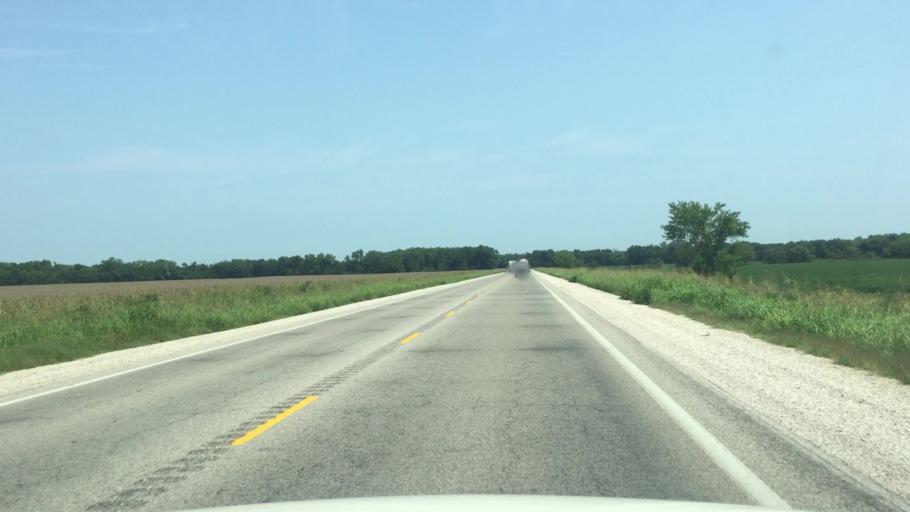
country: US
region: Kansas
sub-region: Montgomery County
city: Cherryvale
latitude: 37.1691
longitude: -95.5765
